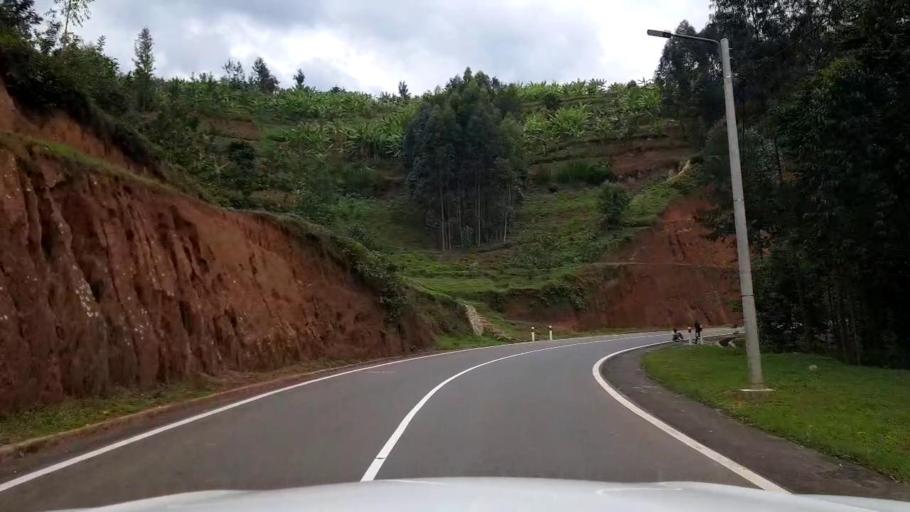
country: RW
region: Western Province
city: Kibuye
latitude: -1.9261
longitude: 29.3700
